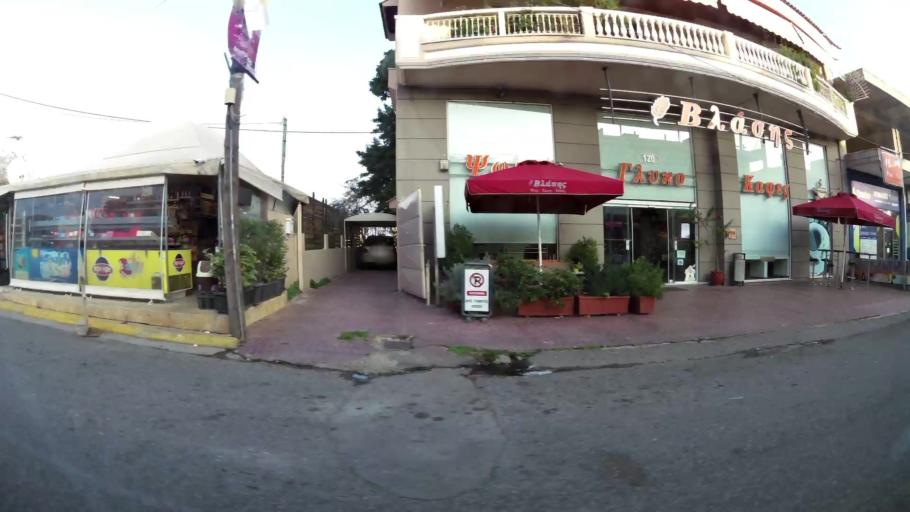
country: GR
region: Attica
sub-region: Nomarchia Anatolikis Attikis
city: Acharnes
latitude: 38.0909
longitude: 23.7379
